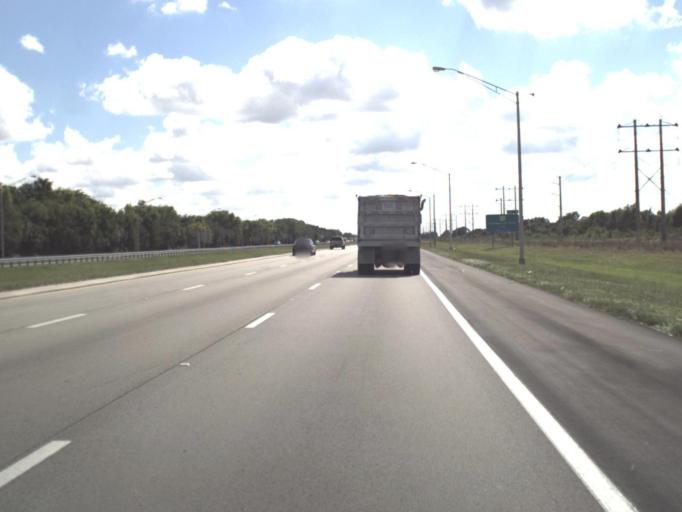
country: US
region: Florida
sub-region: Broward County
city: Tamarac
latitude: 26.2194
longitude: -80.2967
